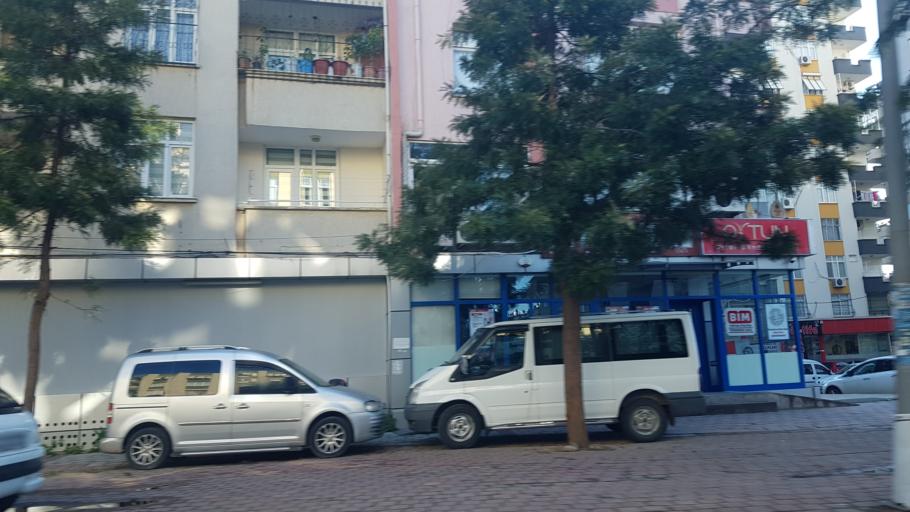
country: TR
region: Adana
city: Adana
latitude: 37.0276
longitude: 35.3106
